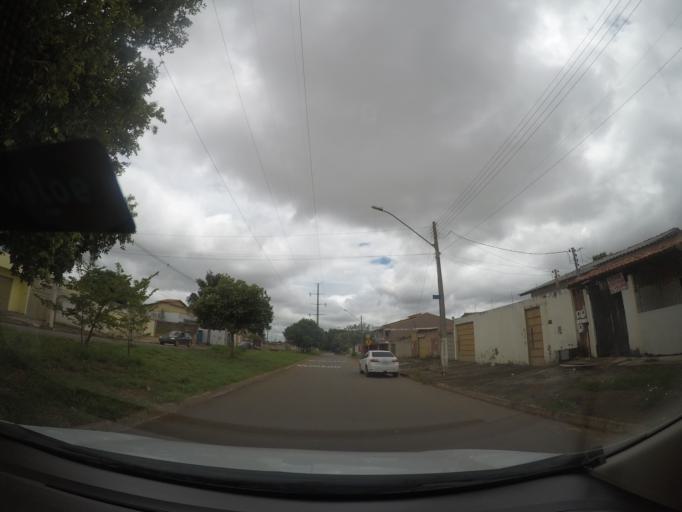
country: BR
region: Goias
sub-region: Goiania
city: Goiania
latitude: -16.7303
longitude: -49.3584
